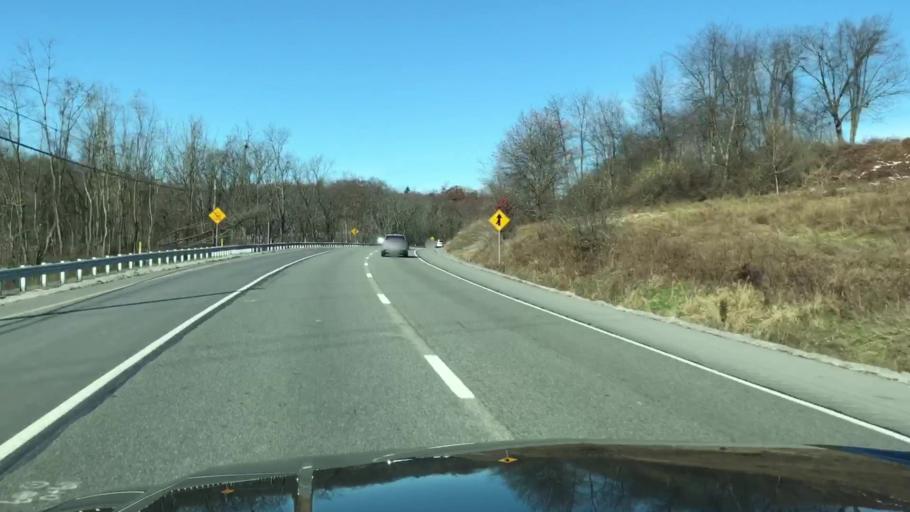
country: US
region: Pennsylvania
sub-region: Snyder County
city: Shamokin Dam
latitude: 40.8763
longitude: -76.8362
